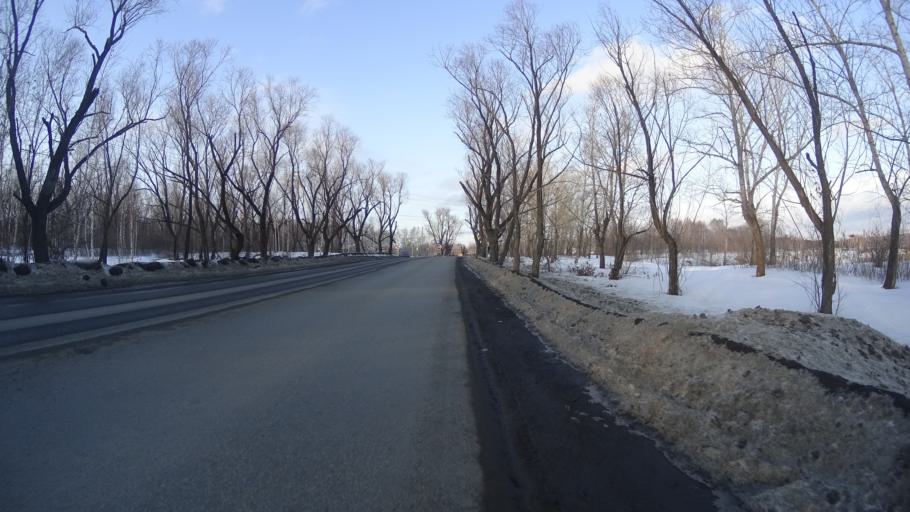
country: RU
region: Chelyabinsk
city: Sargazy
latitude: 55.1434
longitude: 61.2835
